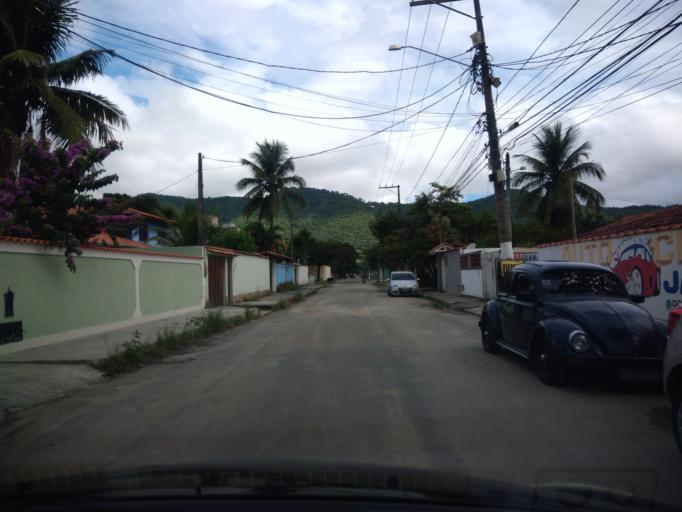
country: BR
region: Rio de Janeiro
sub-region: Niteroi
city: Niteroi
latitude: -22.9289
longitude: -43.0121
